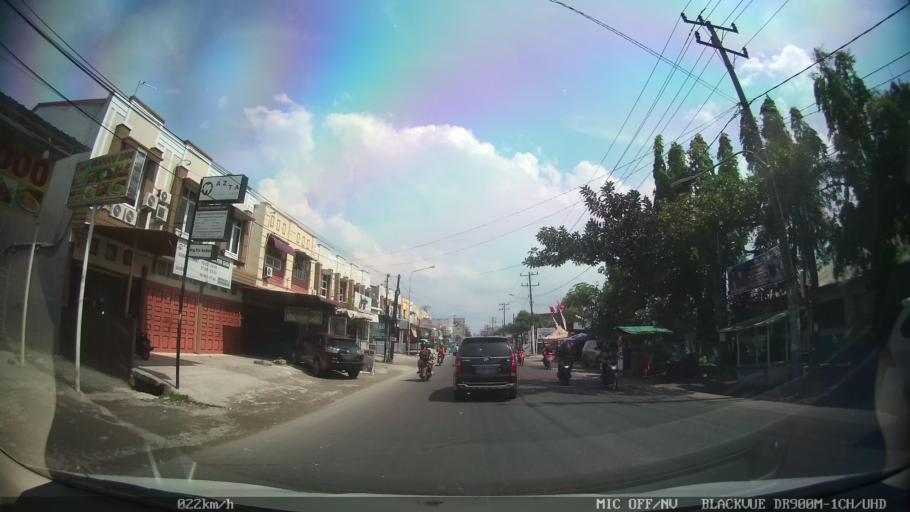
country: ID
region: North Sumatra
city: Medan
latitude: 3.6334
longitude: 98.6603
